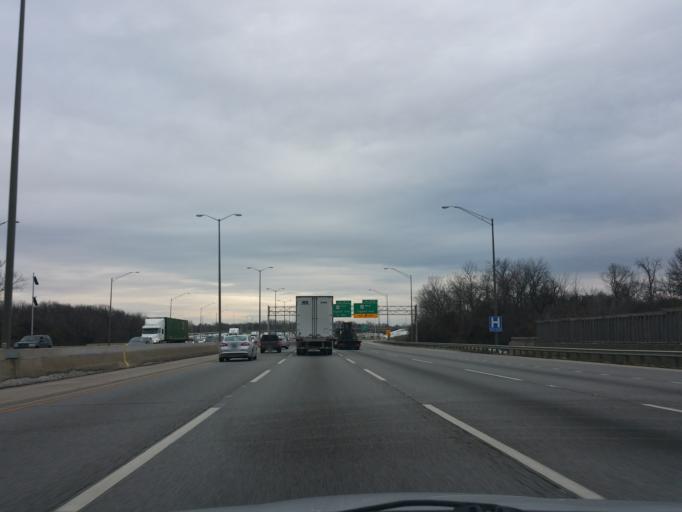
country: US
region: Illinois
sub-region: DuPage County
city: Oak Brook
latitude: 41.8238
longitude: -87.9172
